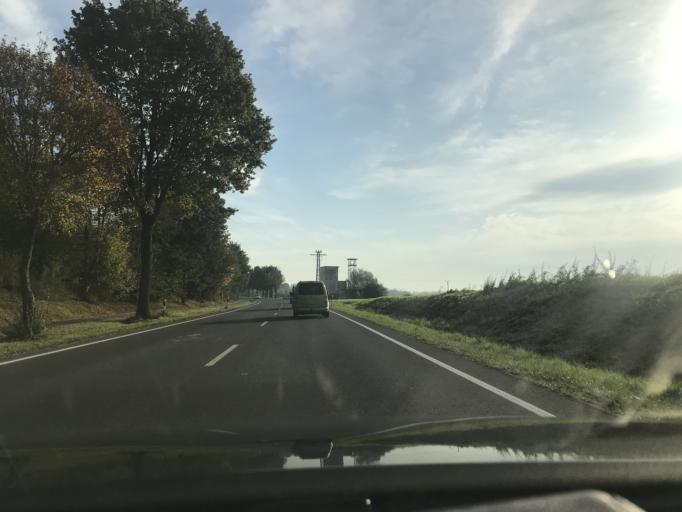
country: DE
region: North Rhine-Westphalia
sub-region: Regierungsbezirk Dusseldorf
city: Nettetal
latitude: 51.3348
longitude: 6.2597
